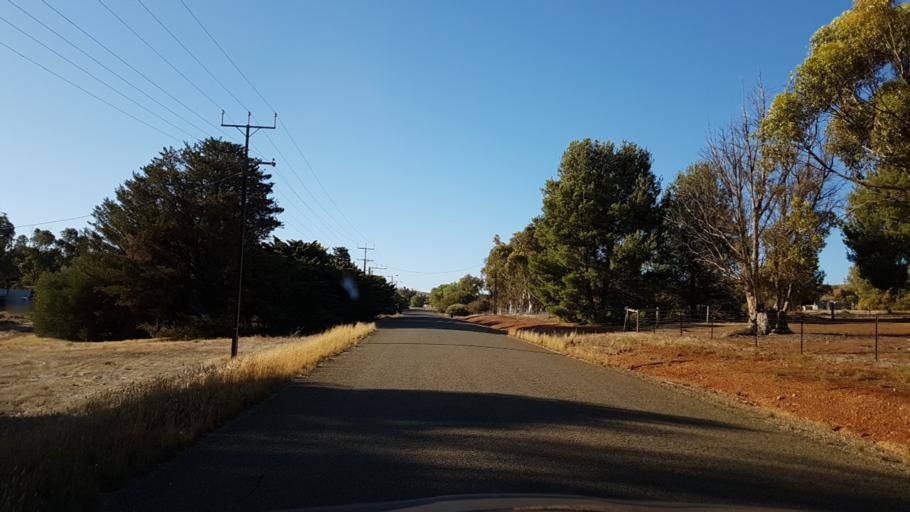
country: AU
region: South Australia
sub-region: Clare and Gilbert Valleys
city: Clare
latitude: -33.6695
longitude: 138.9319
